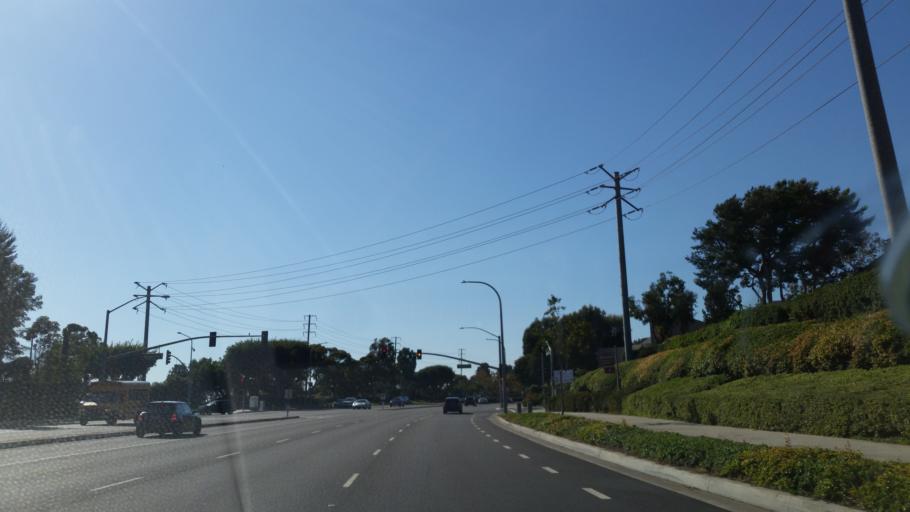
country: US
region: California
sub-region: Orange County
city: San Joaquin Hills
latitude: 33.6074
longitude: -117.8587
